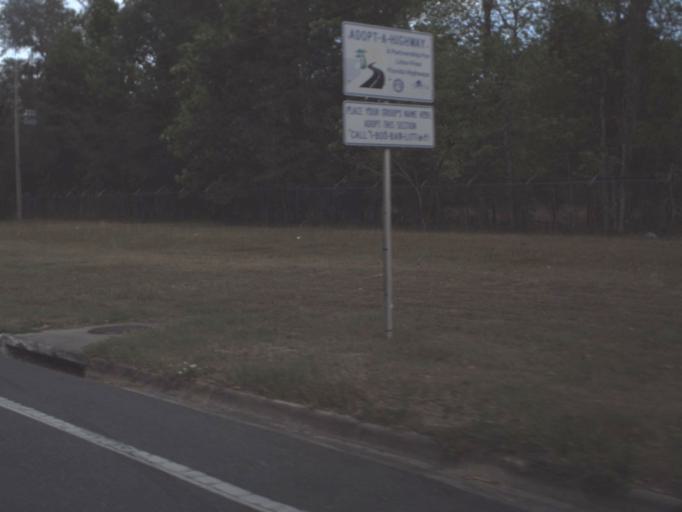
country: US
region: Florida
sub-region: Marion County
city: Ocala
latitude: 29.2191
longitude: -82.0449
